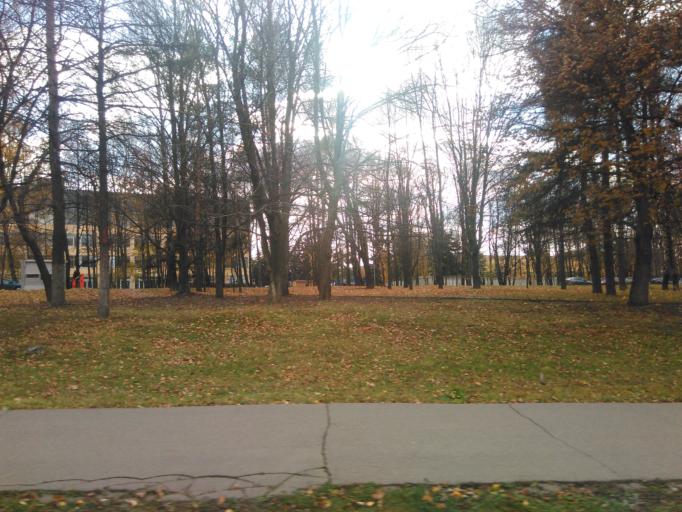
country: RU
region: Moscow
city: Zyuzino
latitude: 55.6498
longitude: 37.5607
